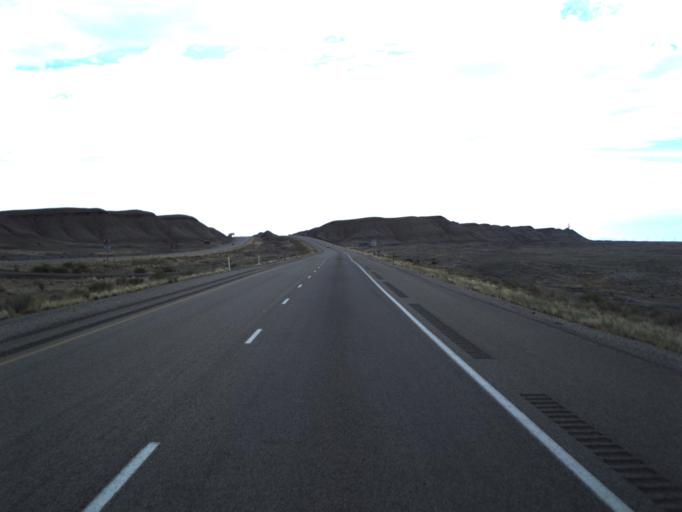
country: US
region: Utah
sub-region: Carbon County
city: East Carbon City
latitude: 38.9734
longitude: -110.1075
